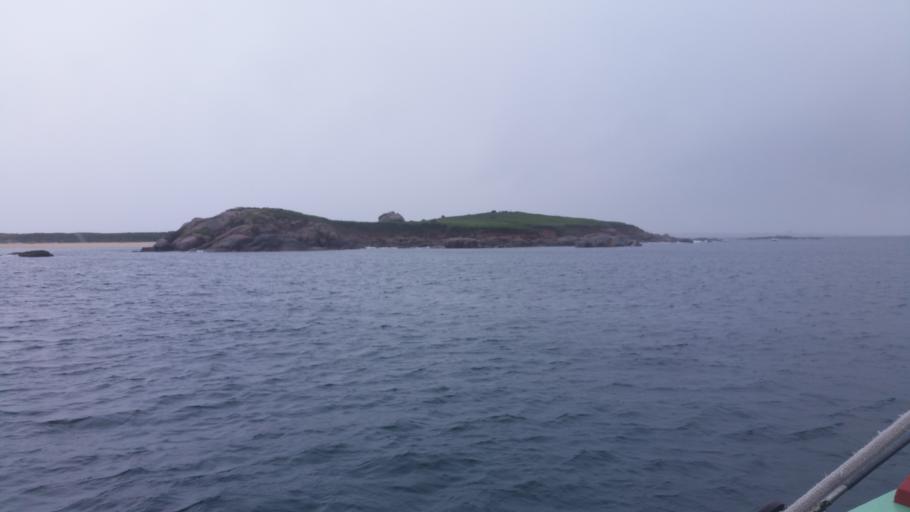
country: FR
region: Brittany
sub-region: Departement du Finistere
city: Carantec
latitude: 48.6969
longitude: -3.9197
